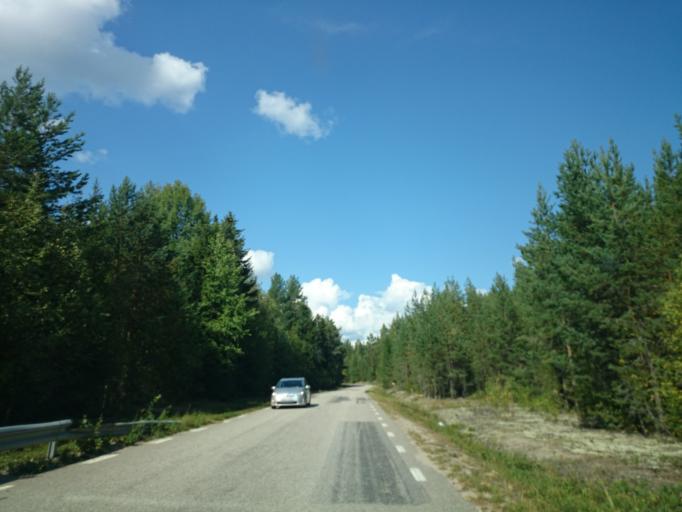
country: SE
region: Gaevleborg
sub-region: Ljusdals Kommun
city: Jaervsoe
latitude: 61.7728
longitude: 16.2134
